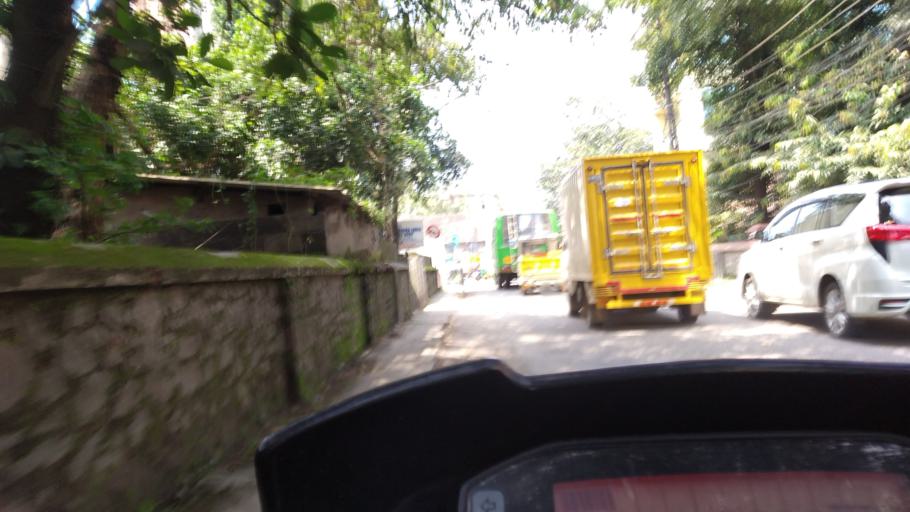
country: IN
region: Kerala
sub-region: Ernakulam
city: Cochin
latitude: 9.9632
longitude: 76.2864
